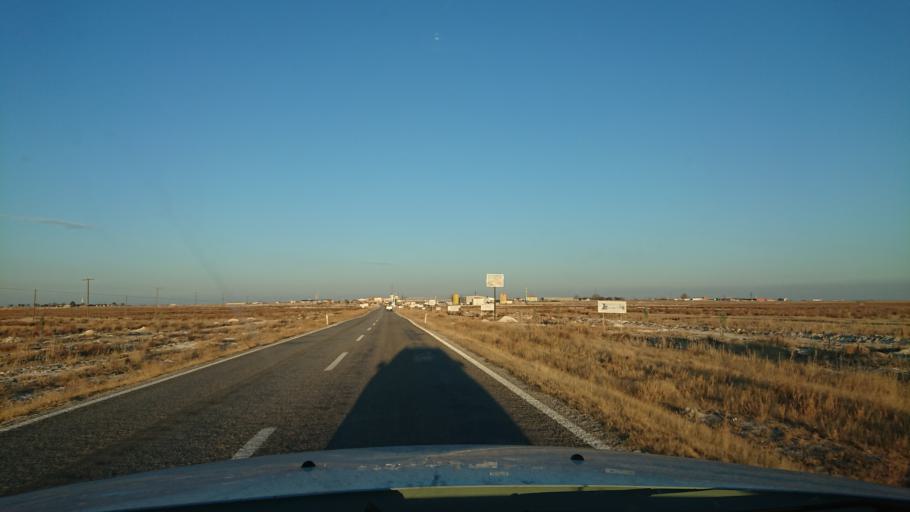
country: TR
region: Aksaray
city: Eskil
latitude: 38.3895
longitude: 33.3863
